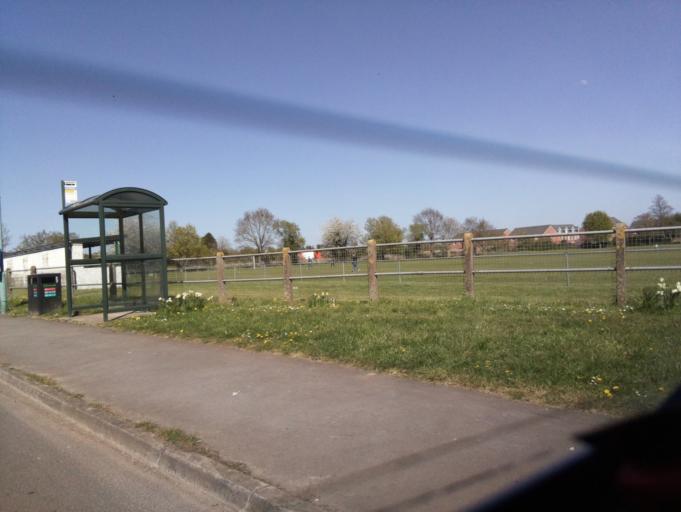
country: GB
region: England
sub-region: Gloucestershire
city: Berkeley
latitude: 51.6959
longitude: -2.4584
